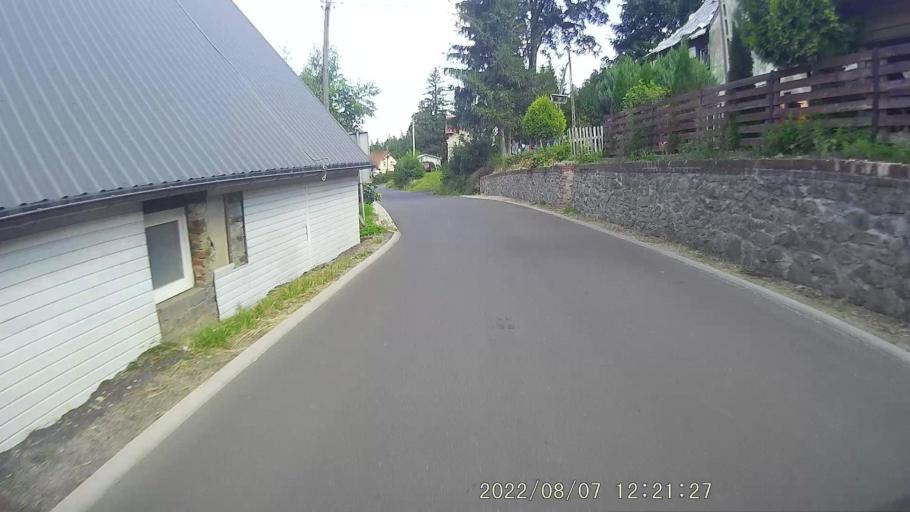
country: PL
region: Lower Silesian Voivodeship
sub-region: Powiat lubanski
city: Swieradow-Zdroj
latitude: 50.9260
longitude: 15.2887
